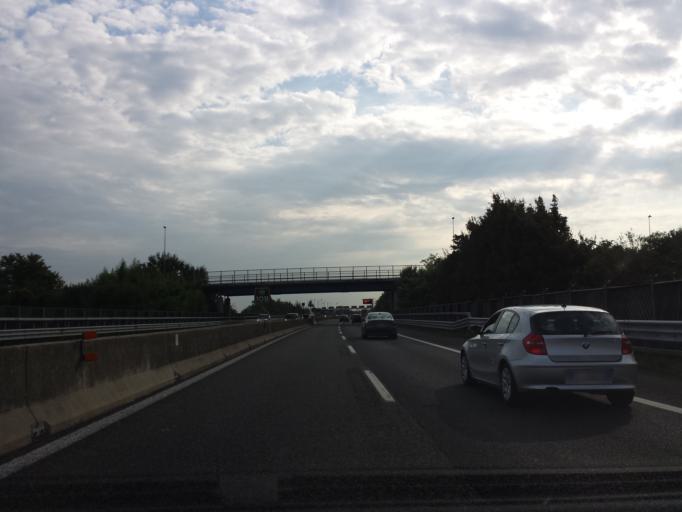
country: IT
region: Veneto
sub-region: Provincia di Padova
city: Mandriola-Sant'Agostino
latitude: 45.3484
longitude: 11.8511
